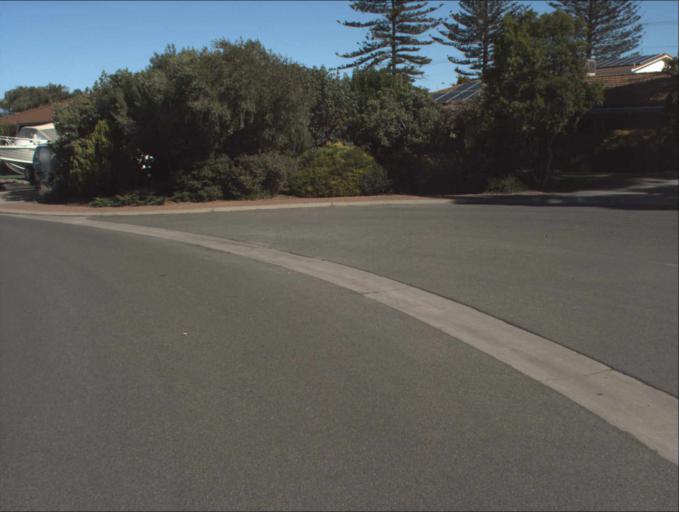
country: AU
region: South Australia
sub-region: Port Adelaide Enfield
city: Birkenhead
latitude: -34.7831
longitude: 138.4902
